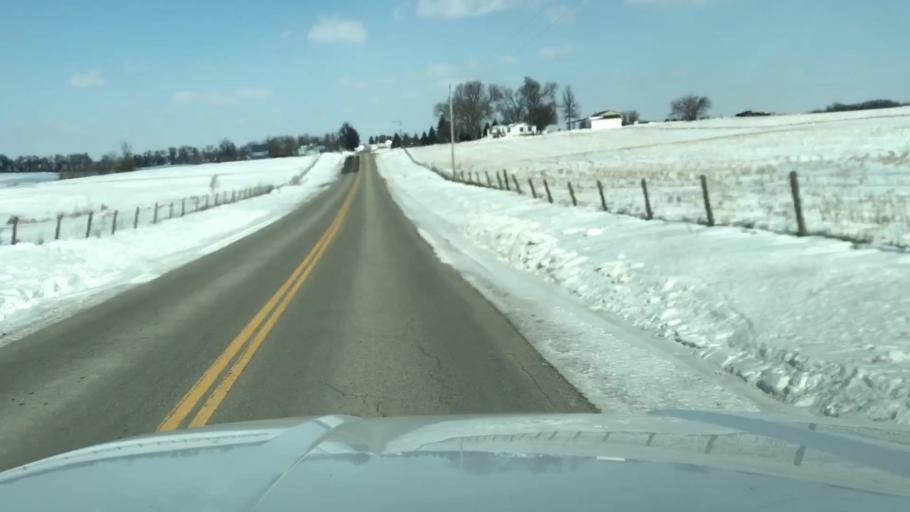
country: US
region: Missouri
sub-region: Nodaway County
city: Maryville
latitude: 40.3631
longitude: -94.7219
